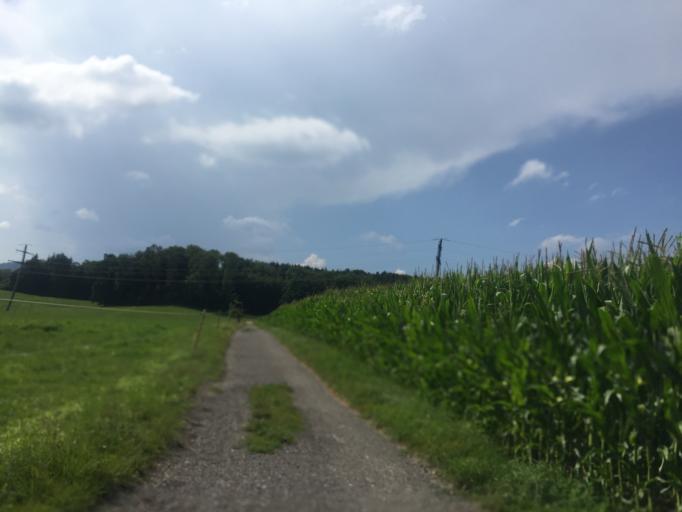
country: CH
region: Bern
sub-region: Bern-Mittelland District
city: Rubigen
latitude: 46.9053
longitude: 7.5295
